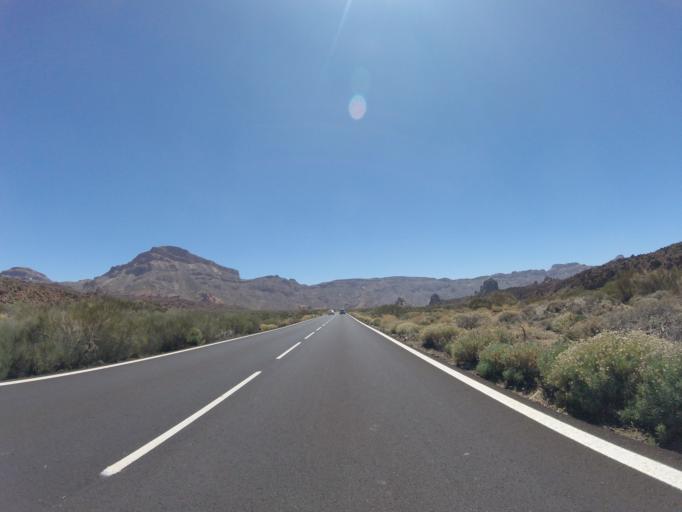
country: ES
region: Canary Islands
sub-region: Provincia de Santa Cruz de Tenerife
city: Vilaflor
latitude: 28.2375
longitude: -16.6299
